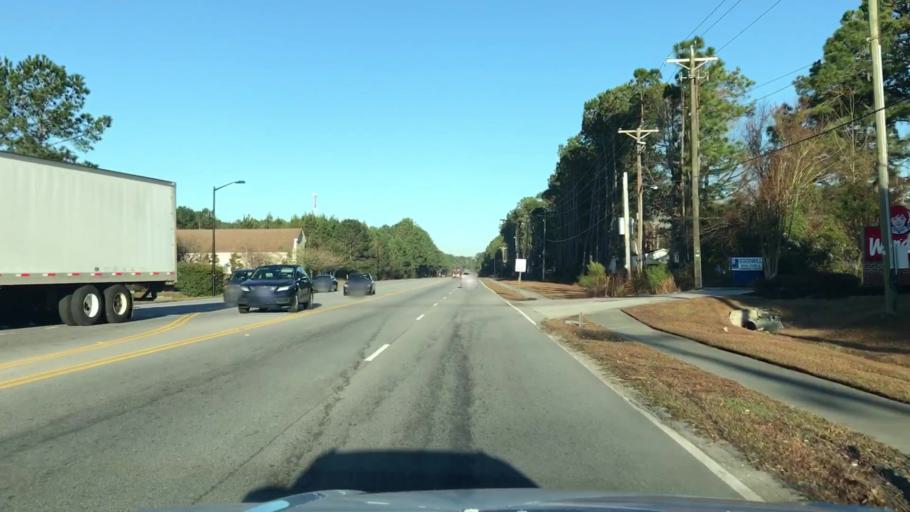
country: US
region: South Carolina
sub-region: Berkeley County
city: Ladson
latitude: 32.9186
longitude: -80.1030
